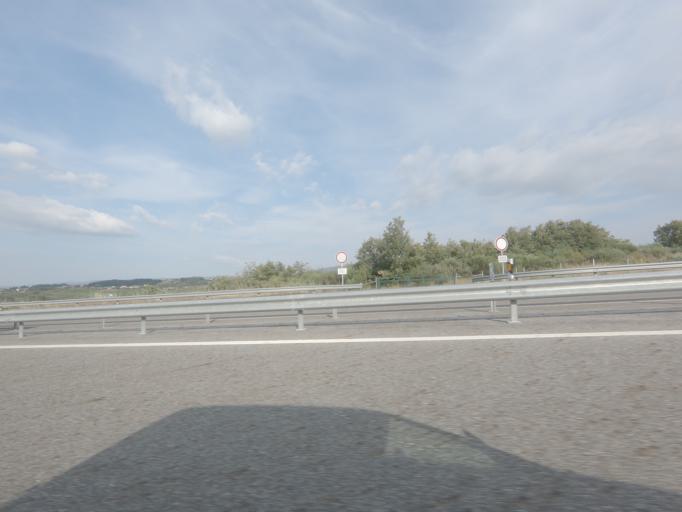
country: PT
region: Vila Real
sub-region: Chaves
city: Chaves
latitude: 41.7344
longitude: -7.5290
